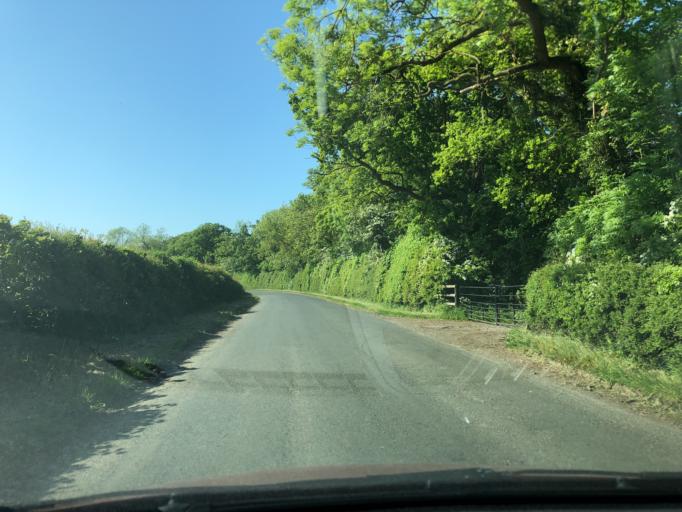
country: GB
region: England
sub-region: North Yorkshire
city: Northallerton
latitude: 54.3160
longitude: -1.3749
